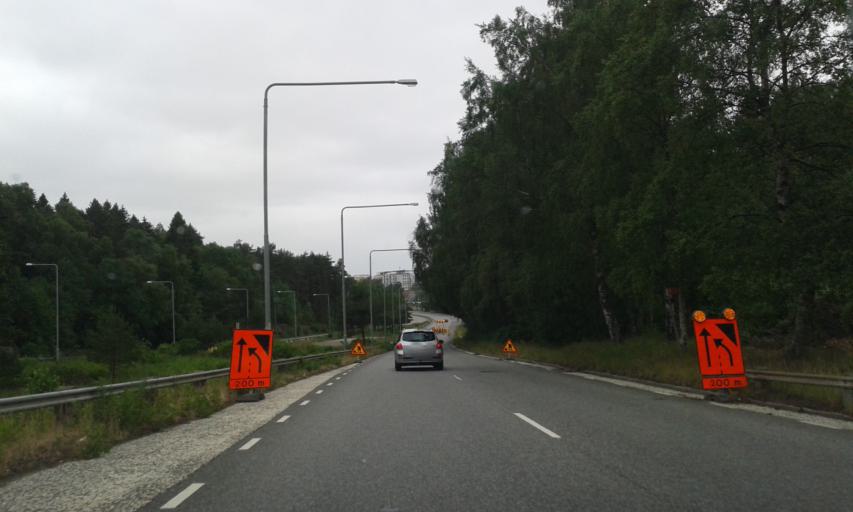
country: SE
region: Vaestra Goetaland
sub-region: Goteborg
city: Eriksbo
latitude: 57.7551
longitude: 12.0432
